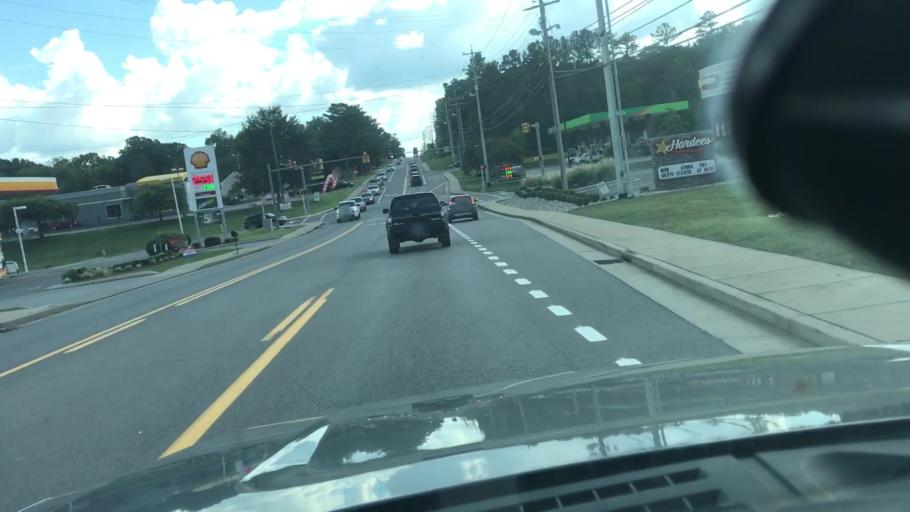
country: US
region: Tennessee
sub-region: Williamson County
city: Fairview
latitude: 35.9739
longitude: -87.1282
